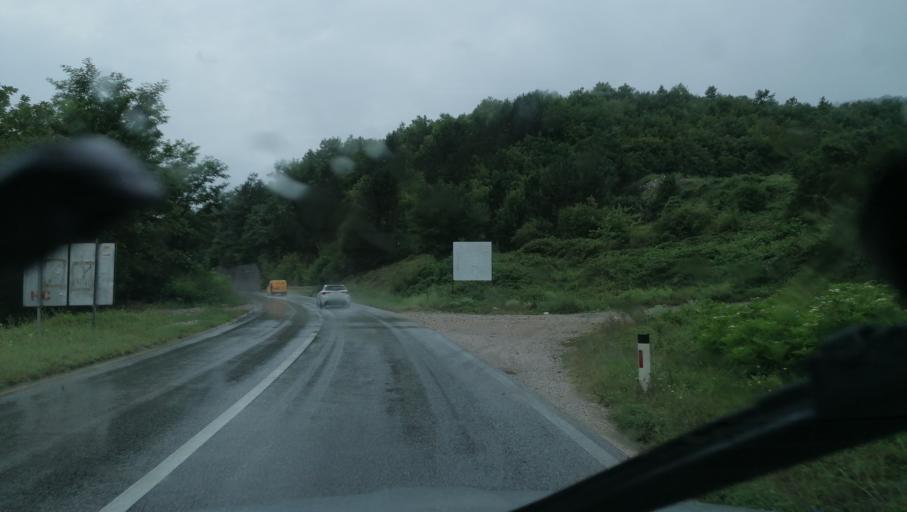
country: BA
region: Federation of Bosnia and Herzegovina
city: Gorazde
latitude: 43.6788
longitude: 19.0530
